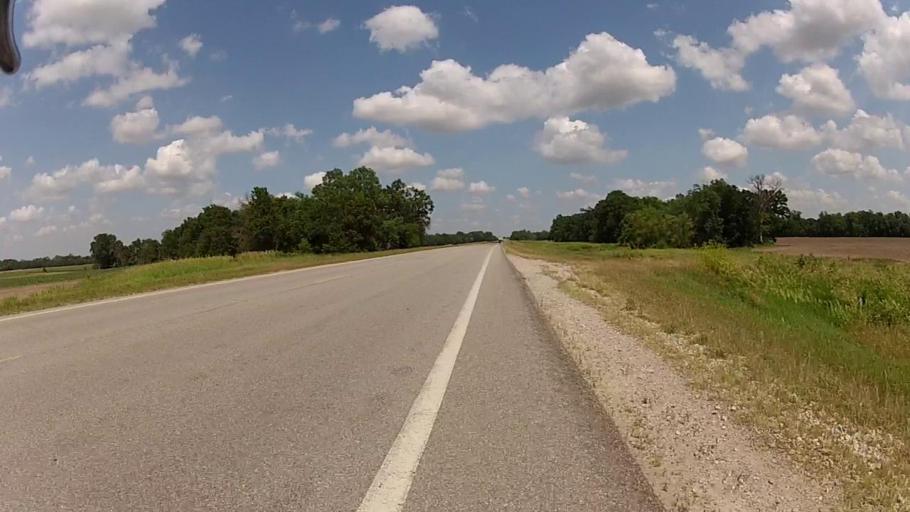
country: US
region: Kansas
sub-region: Labette County
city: Altamont
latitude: 37.1937
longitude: -95.2039
